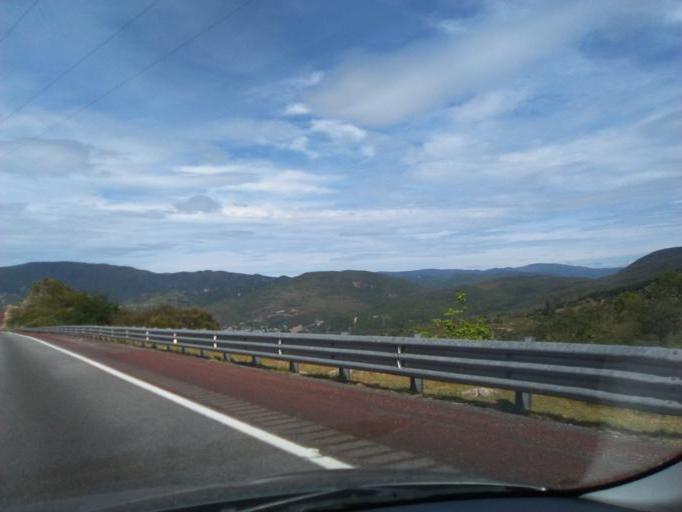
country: MX
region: Guerrero
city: Mazatlan
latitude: 17.4605
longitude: -99.4753
